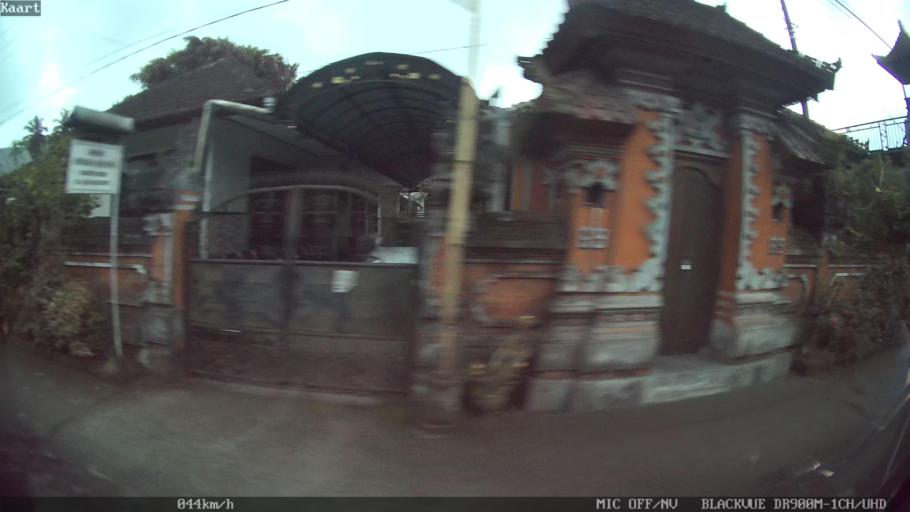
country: ID
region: Bali
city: Banjar Kubu
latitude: -8.4285
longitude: 115.4280
